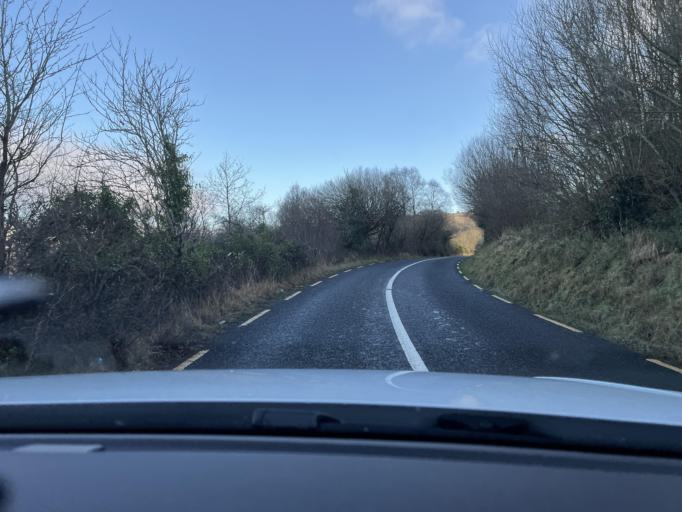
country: IE
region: Connaught
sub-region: County Leitrim
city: Manorhamilton
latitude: 54.2014
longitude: -7.9585
